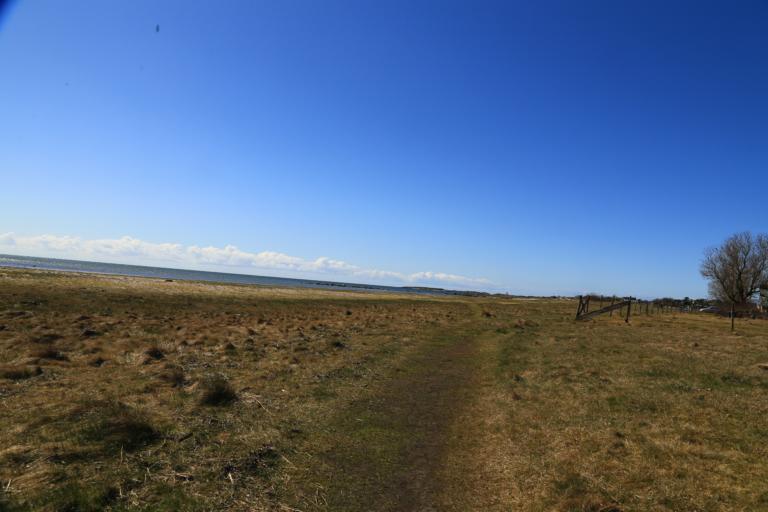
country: SE
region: Halland
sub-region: Varbergs Kommun
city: Traslovslage
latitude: 57.0691
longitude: 12.2697
